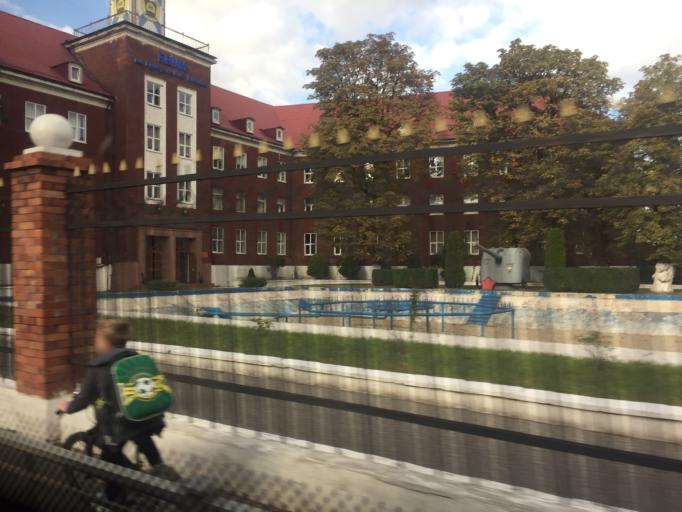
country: RU
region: Kaliningrad
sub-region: Gorod Kaliningrad
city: Kaliningrad
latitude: 54.7335
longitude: 20.4854
